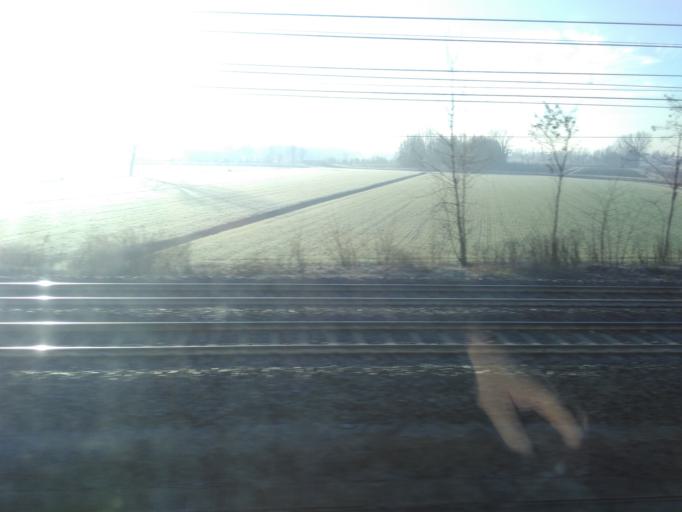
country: IT
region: Veneto
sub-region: Provincia di Venezia
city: Arino
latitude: 45.4469
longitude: 12.0385
